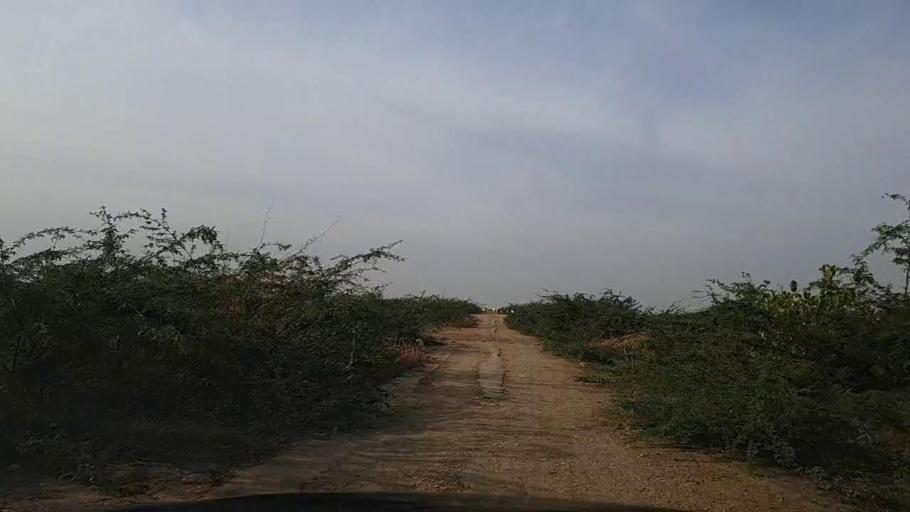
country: PK
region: Sindh
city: Gharo
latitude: 24.7844
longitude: 67.5600
